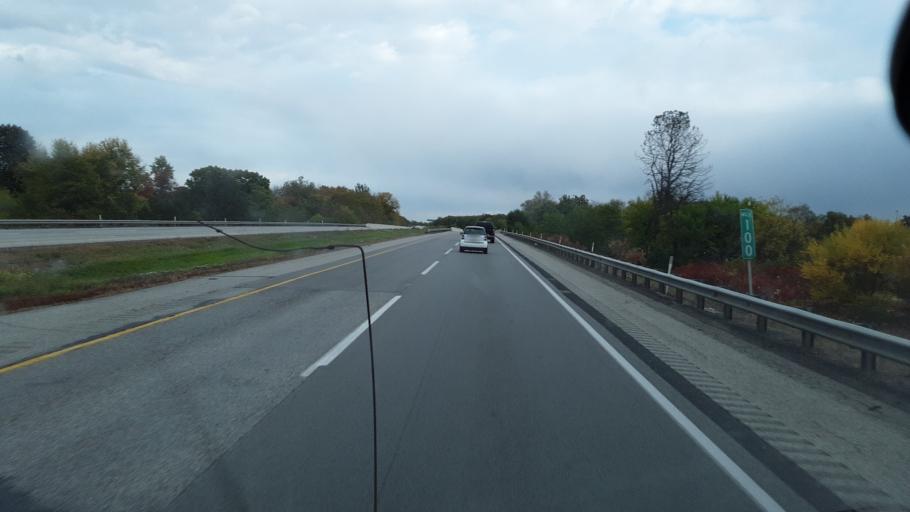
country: US
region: Indiana
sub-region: Elkhart County
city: Bristol
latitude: 41.7356
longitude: -85.8146
